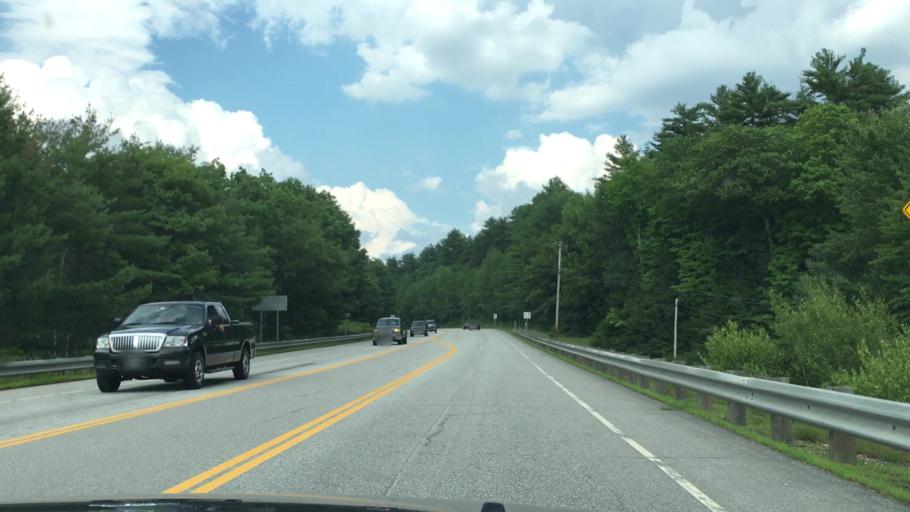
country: US
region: New Hampshire
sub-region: Belknap County
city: Gilford
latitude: 43.5800
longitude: -71.3925
